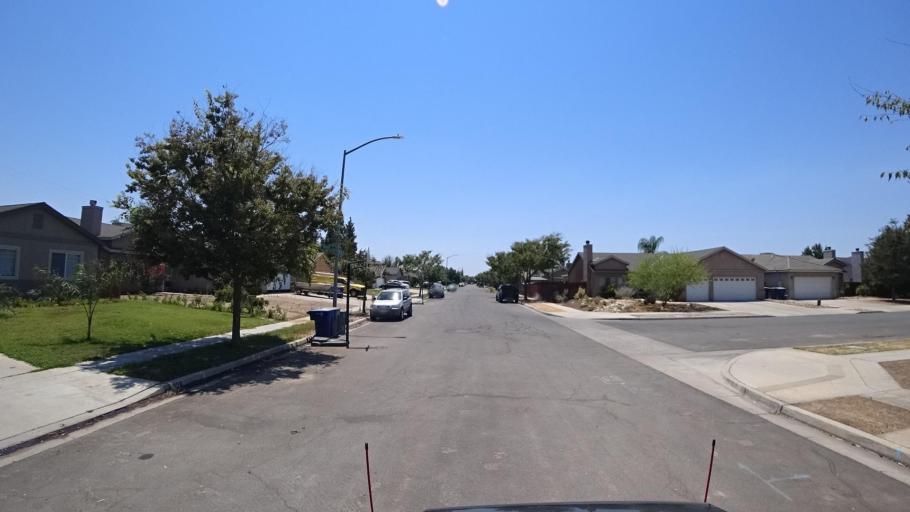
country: US
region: California
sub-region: Fresno County
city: Sunnyside
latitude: 36.7435
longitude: -119.6715
